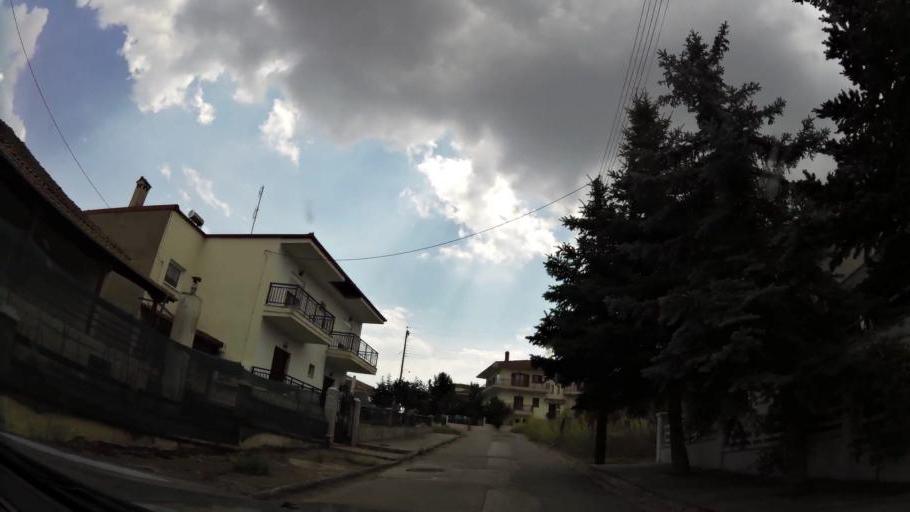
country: GR
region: West Macedonia
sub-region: Nomos Kozanis
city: Koila
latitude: 40.3276
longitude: 21.8239
